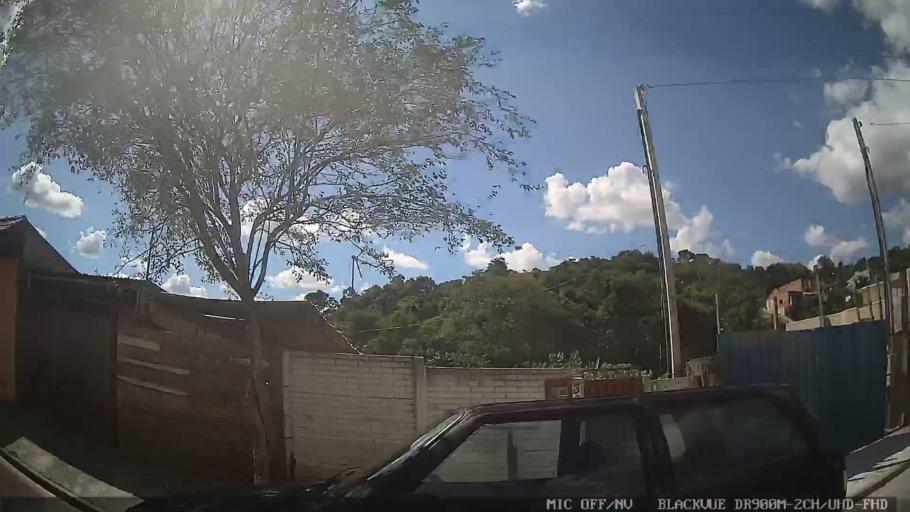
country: BR
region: Sao Paulo
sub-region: Atibaia
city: Atibaia
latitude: -23.1475
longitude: -46.5656
